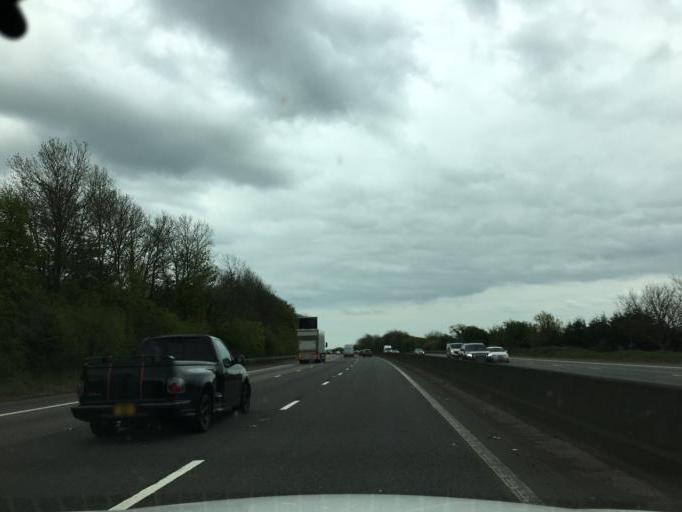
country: GB
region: England
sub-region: Wiltshire
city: Aldbourne
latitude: 51.4927
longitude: -1.5803
